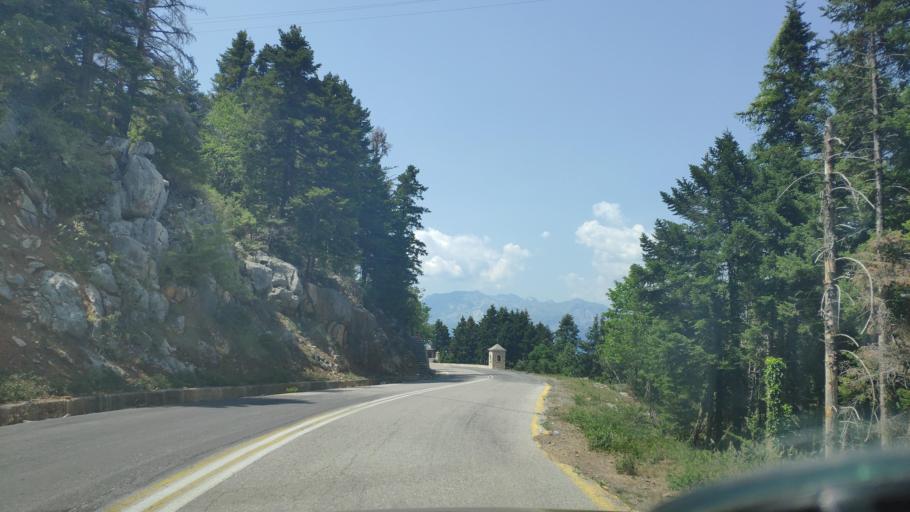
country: GR
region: Epirus
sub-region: Nomos Artas
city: Ano Kalentini
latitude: 39.2679
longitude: 21.2586
